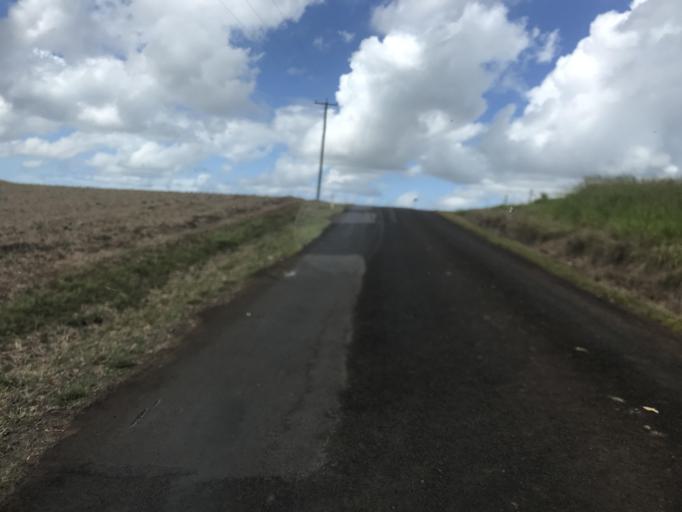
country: AU
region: Queensland
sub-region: Cassowary Coast
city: Innisfail
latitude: -17.5530
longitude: 145.8846
